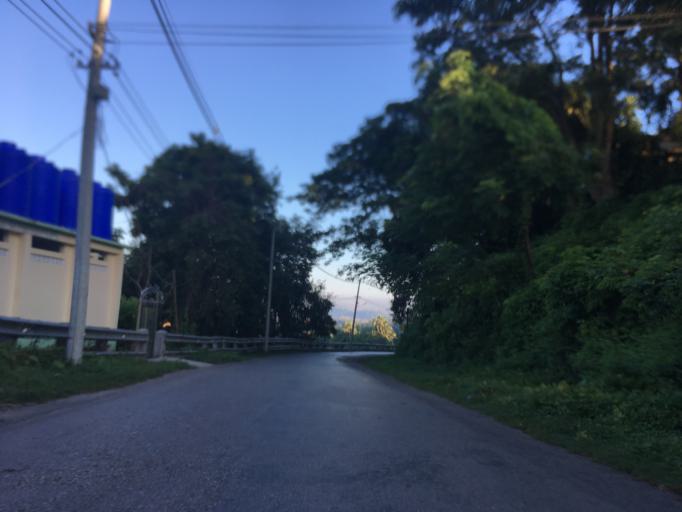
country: MM
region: Mon
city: Mawlamyine
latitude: 16.4863
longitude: 97.6281
